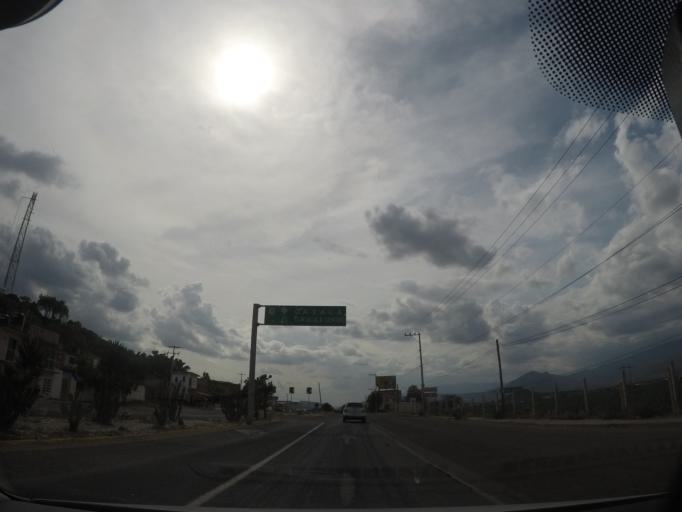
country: MX
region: Oaxaca
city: Tlacolula de Matamoros
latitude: 16.9678
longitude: -96.4849
